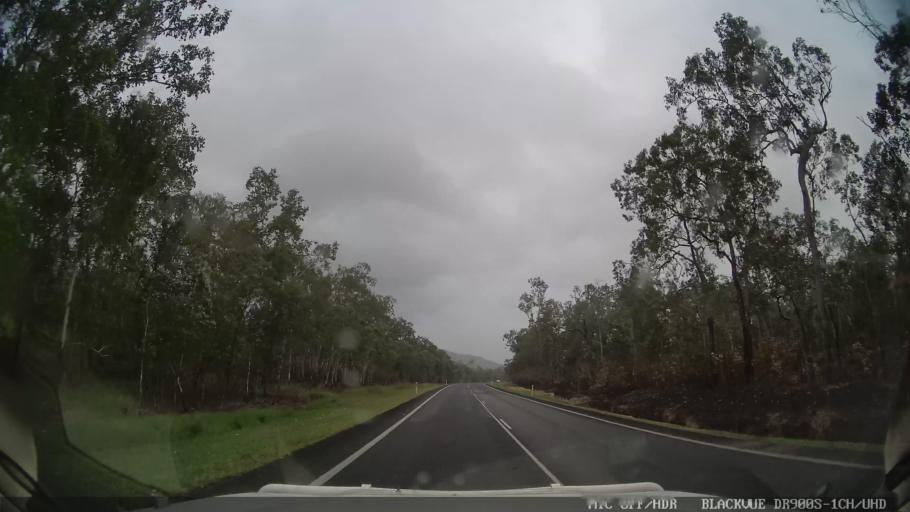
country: AU
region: Queensland
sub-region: Hinchinbrook
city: Ingham
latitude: -18.4402
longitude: 146.1396
